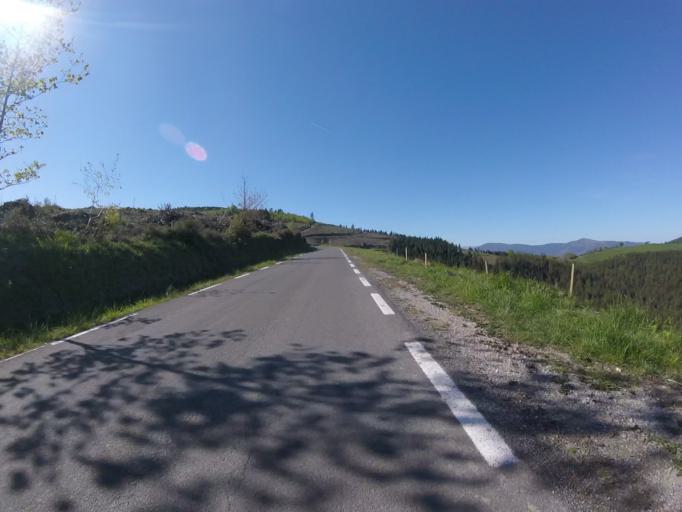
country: ES
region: Basque Country
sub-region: Provincia de Guipuzcoa
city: Errezil
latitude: 43.2043
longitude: -2.1981
